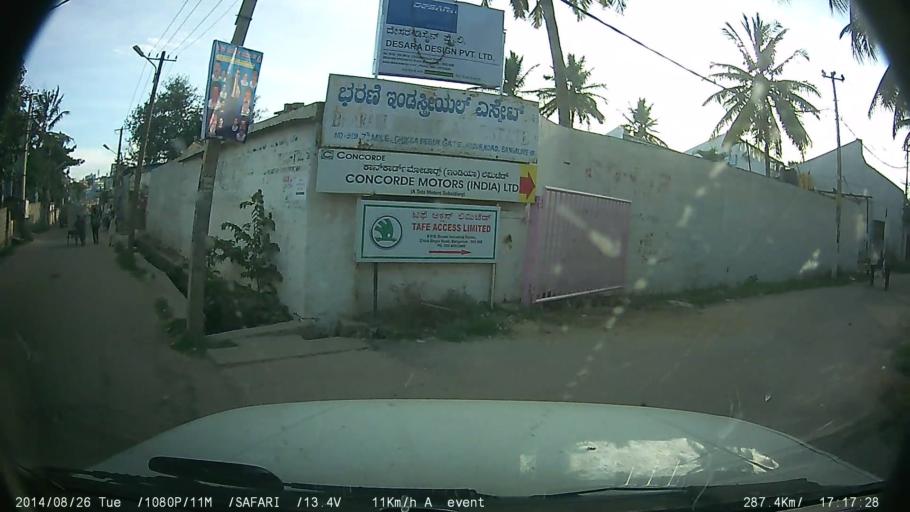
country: IN
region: Karnataka
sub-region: Bangalore Urban
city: Bangalore
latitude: 12.8867
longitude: 77.6395
